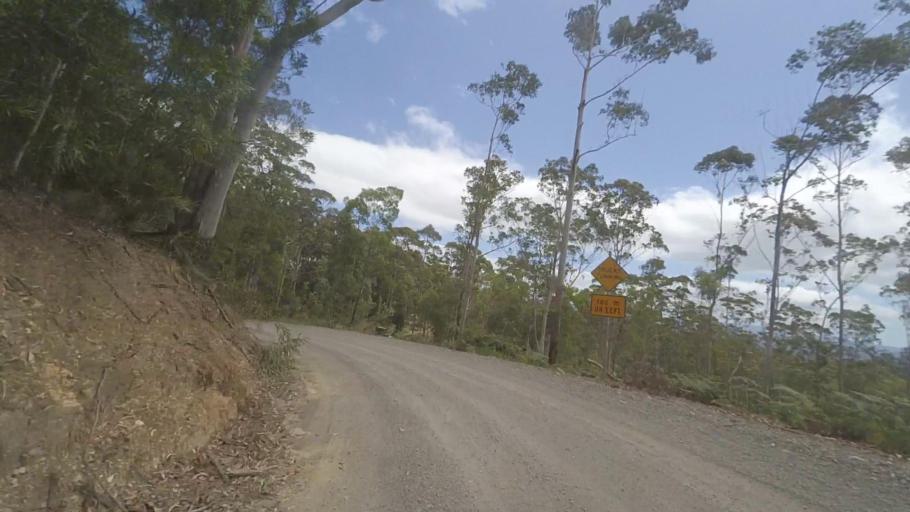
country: AU
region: New South Wales
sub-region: Shoalhaven Shire
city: Milton
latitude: -35.4420
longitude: 150.2960
